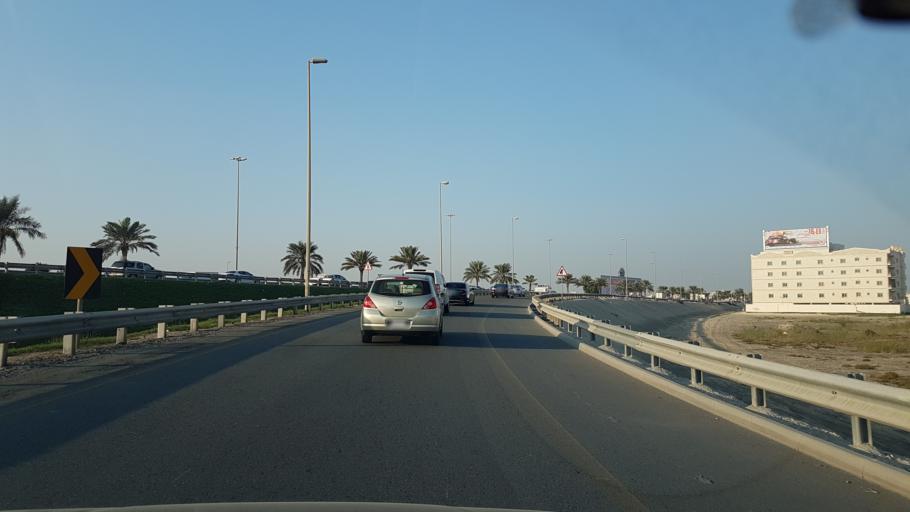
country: BH
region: Northern
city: Madinat `Isa
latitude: 26.1892
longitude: 50.5049
